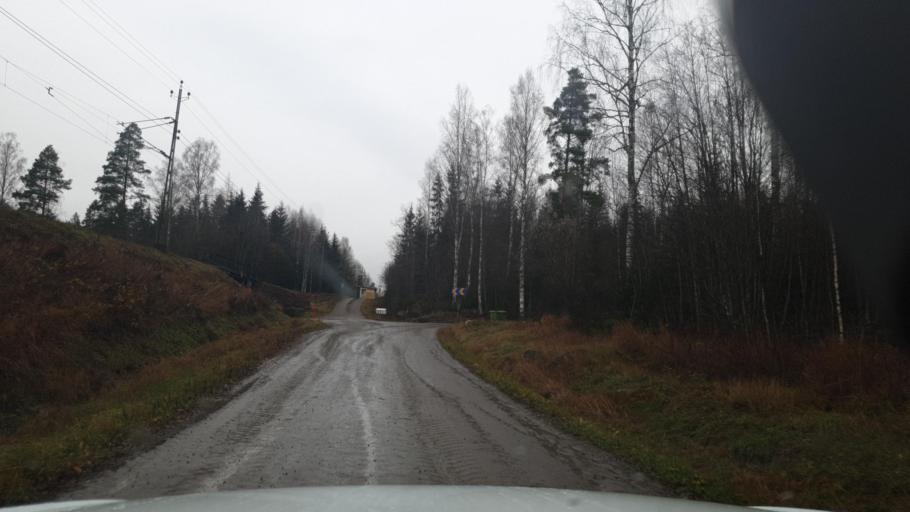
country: SE
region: Vaermland
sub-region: Eda Kommun
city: Amotfors
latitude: 59.8254
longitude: 12.3636
